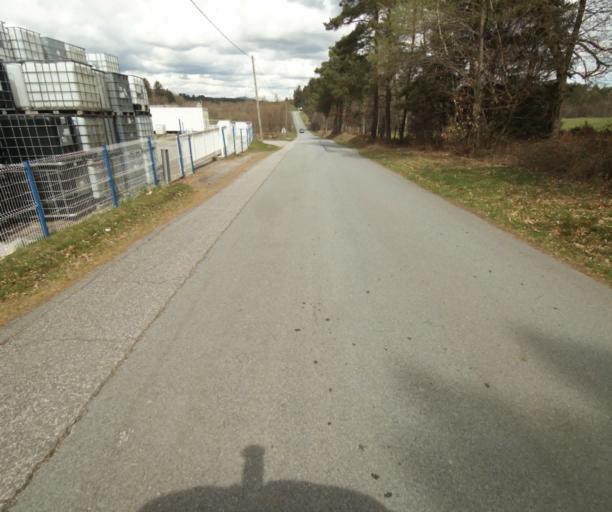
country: FR
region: Limousin
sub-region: Departement de la Correze
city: Correze
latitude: 45.3421
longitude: 1.9470
